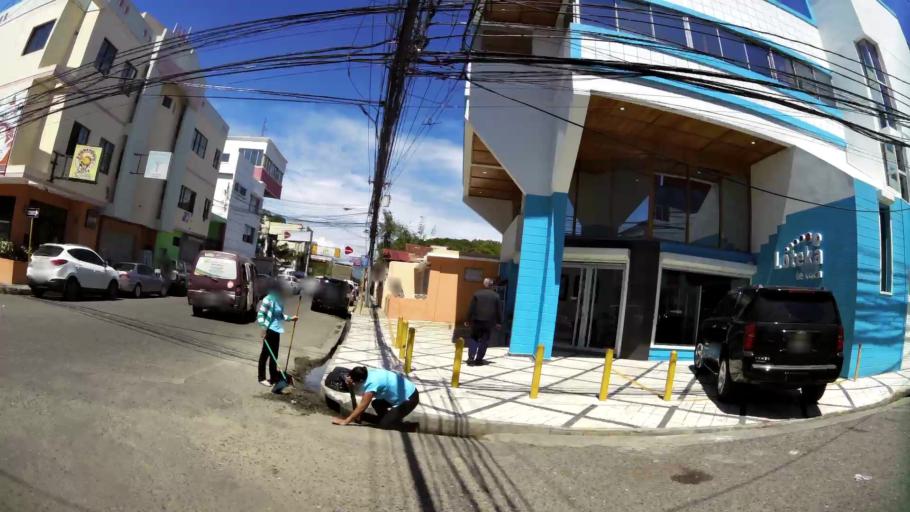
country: DO
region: Santiago
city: Santiago de los Caballeros
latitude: 19.4544
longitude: -70.6984
